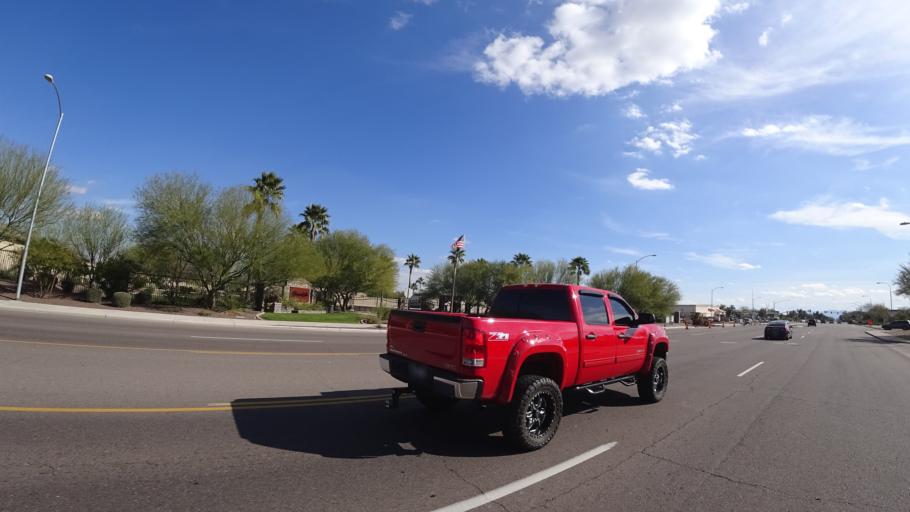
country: US
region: Arizona
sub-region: Maricopa County
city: Peoria
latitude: 33.6129
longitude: -112.2200
